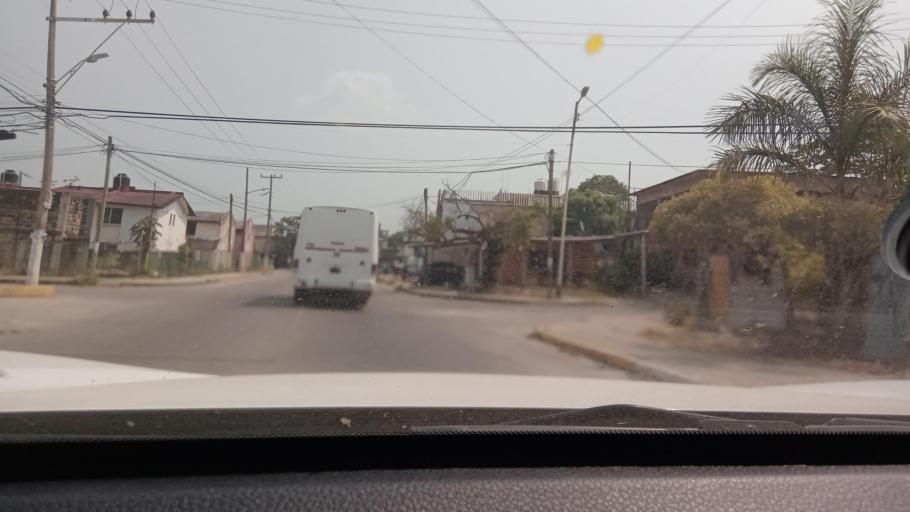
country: MX
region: Veracruz
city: Minatitlan
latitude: 17.9858
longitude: -94.5690
